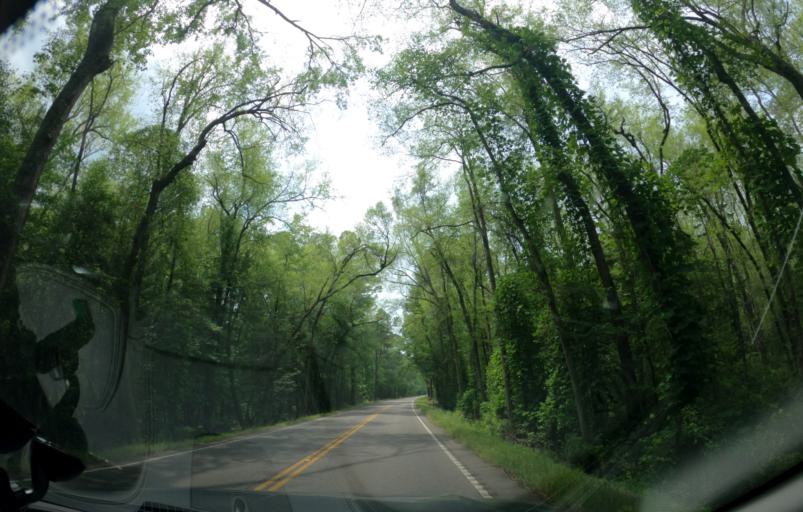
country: US
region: South Carolina
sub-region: Barnwell County
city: Williston
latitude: 33.5538
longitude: -81.4854
